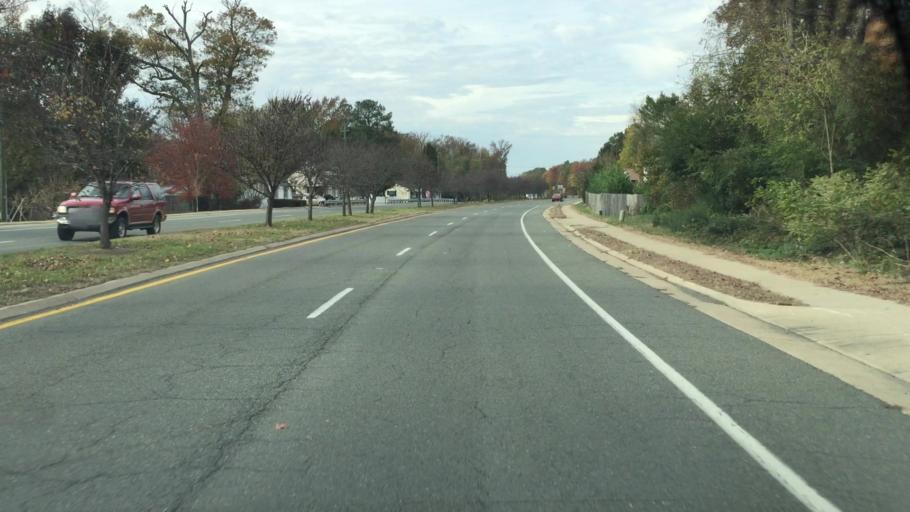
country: US
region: Virginia
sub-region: Chesterfield County
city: Bon Air
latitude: 37.5101
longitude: -77.5861
